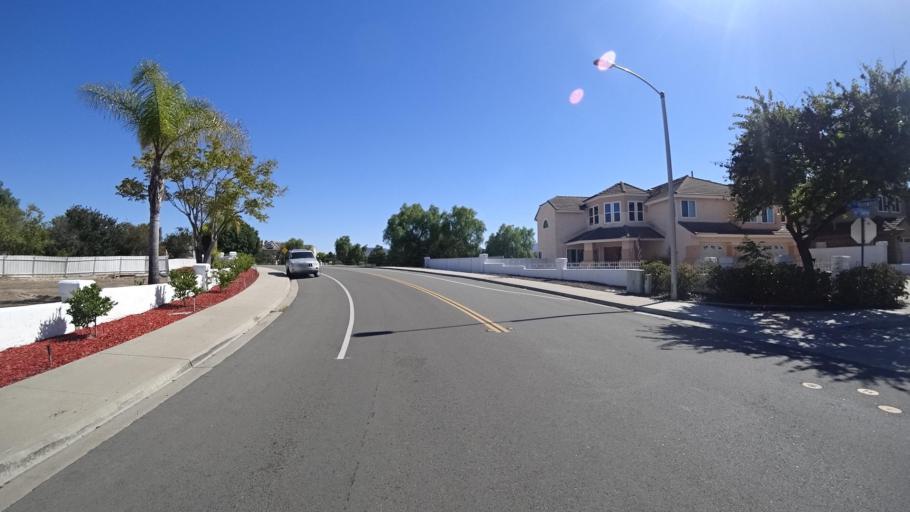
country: US
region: California
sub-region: San Diego County
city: Bonita
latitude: 32.6531
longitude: -116.9870
